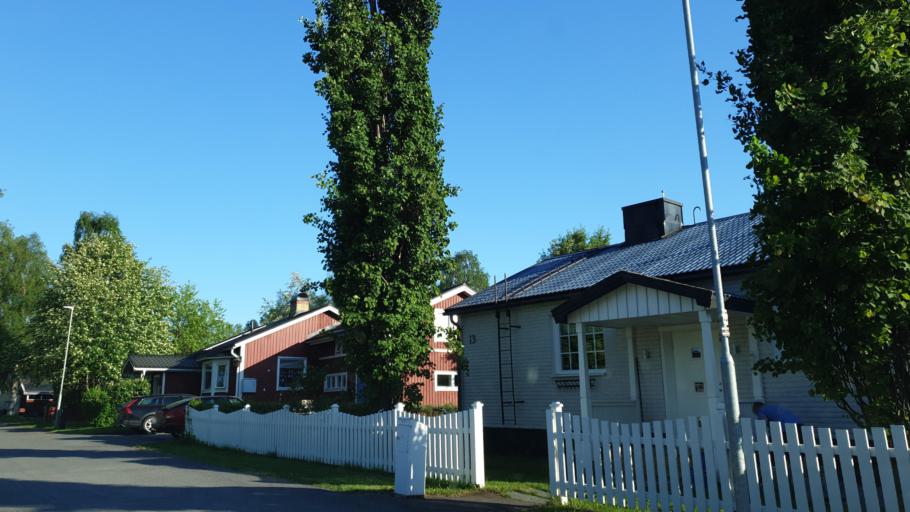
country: SE
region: Norrbotten
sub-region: Lulea Kommun
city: Gammelstad
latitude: 65.6429
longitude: 22.0266
